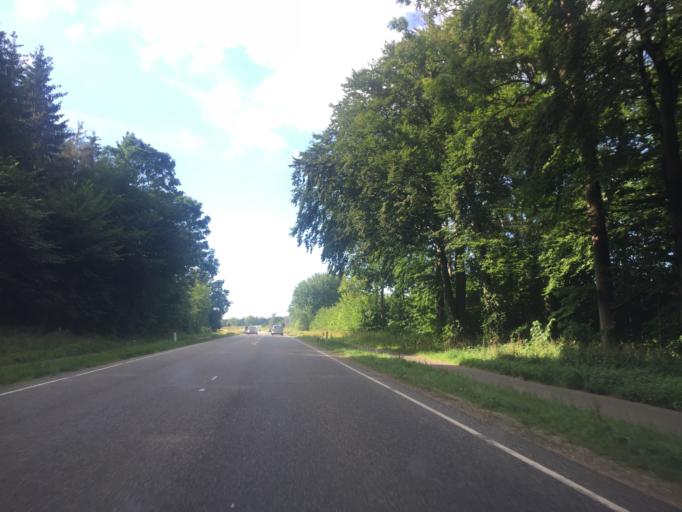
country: DK
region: Zealand
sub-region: Guldborgsund Kommune
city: Nykobing Falster
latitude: 54.7424
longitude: 11.9174
